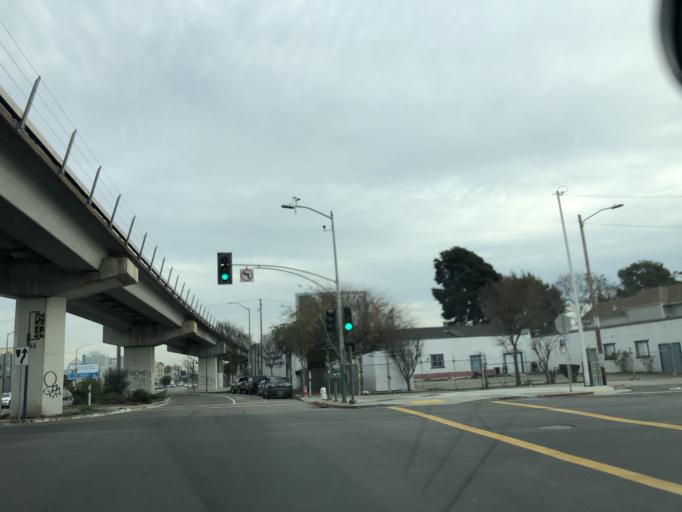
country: US
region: California
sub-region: Alameda County
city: Oakland
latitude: 37.8060
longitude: -122.2985
